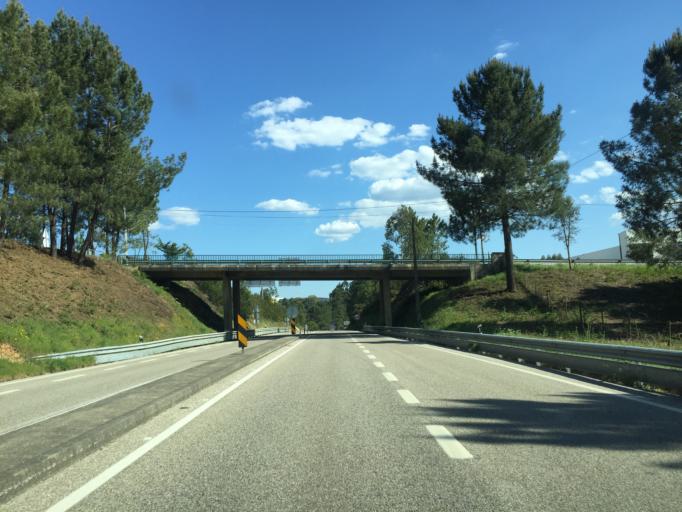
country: PT
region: Leiria
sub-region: Pedrogao Grande
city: Pedrogao Grande
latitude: 39.9231
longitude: -8.1563
